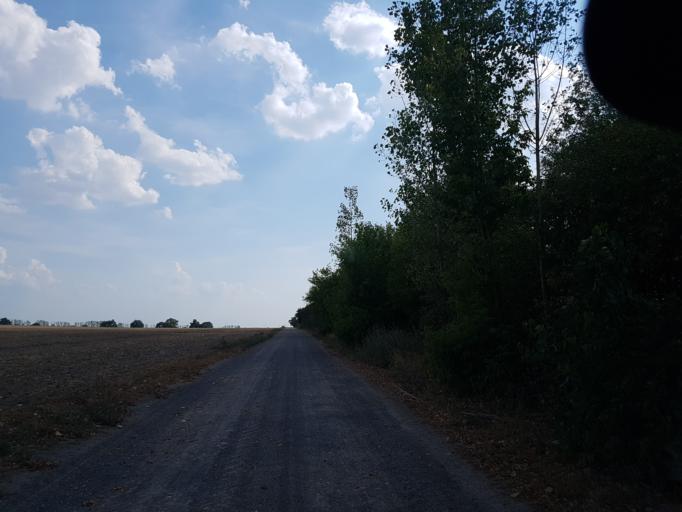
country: DE
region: Brandenburg
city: Treuenbrietzen
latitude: 52.0030
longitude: 12.8690
